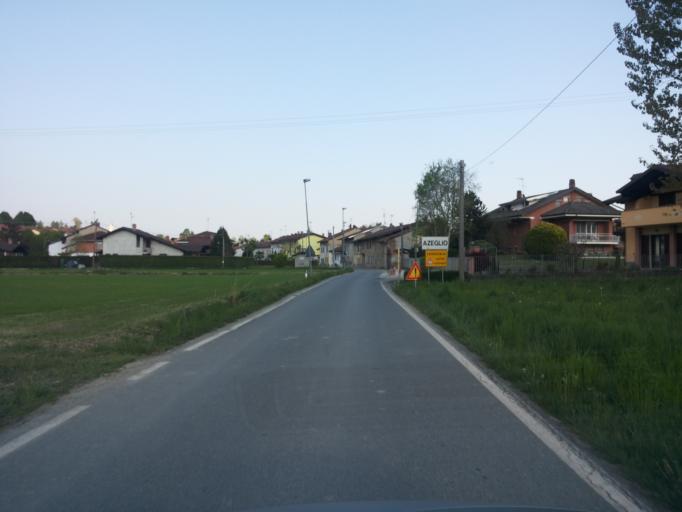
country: IT
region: Piedmont
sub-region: Provincia di Torino
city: Azeglio
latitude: 45.4212
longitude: 7.9793
